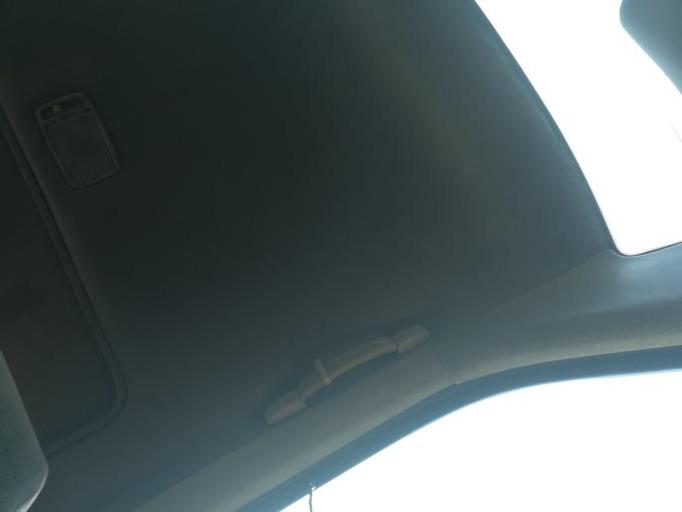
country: NG
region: Lagos
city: Ikorodu
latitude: 6.6447
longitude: 3.5572
